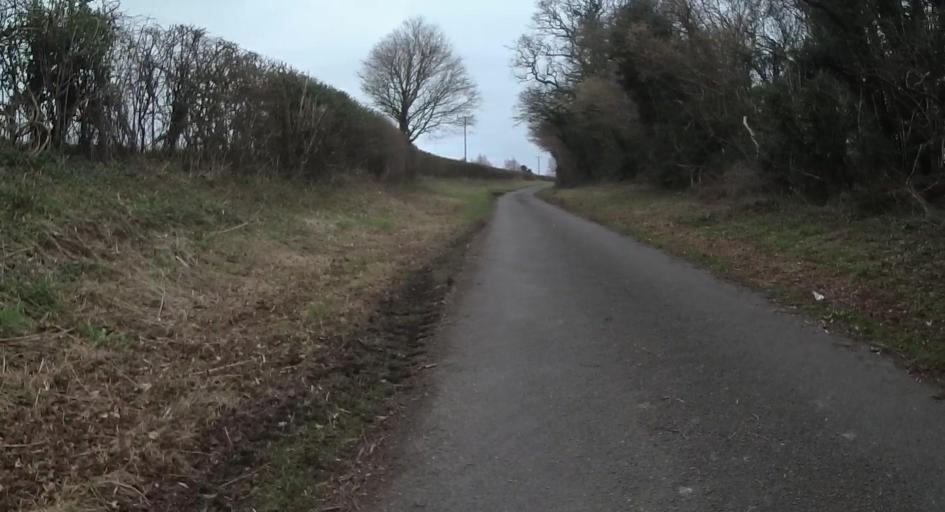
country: GB
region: England
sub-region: Hampshire
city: Highclere
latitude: 51.3247
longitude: -1.3175
